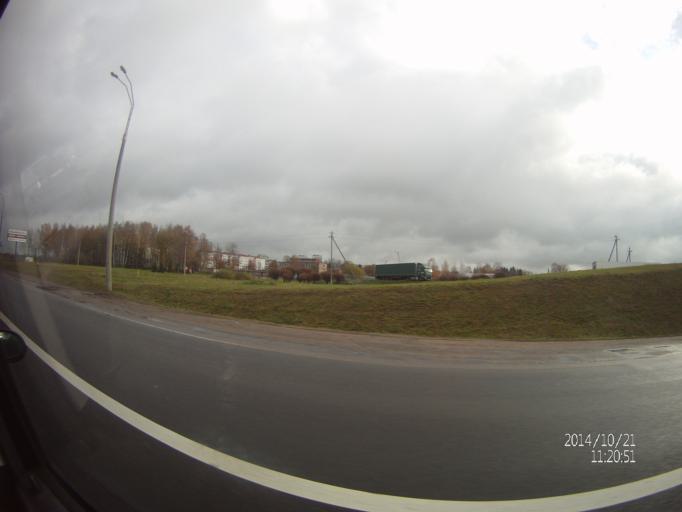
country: BY
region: Minsk
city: Zhdanovichy
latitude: 53.9065
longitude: 27.4077
